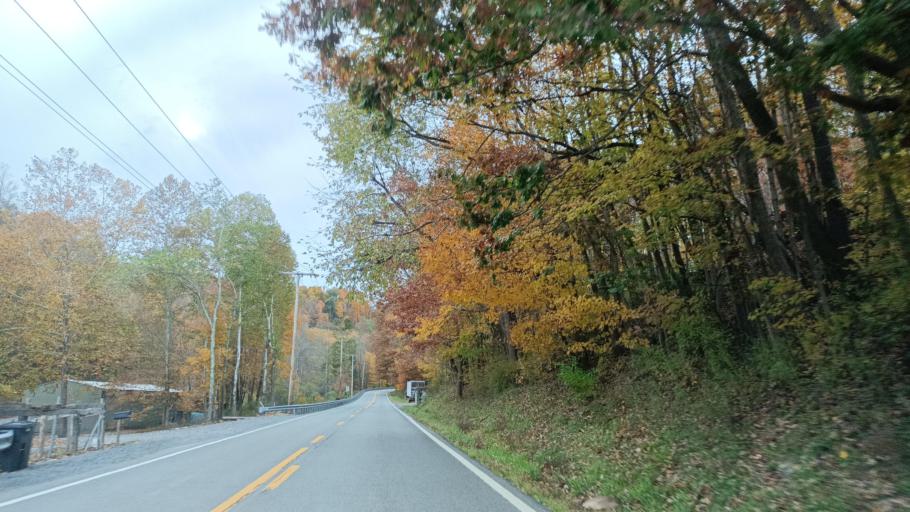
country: US
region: West Virginia
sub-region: Taylor County
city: Grafton
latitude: 39.3300
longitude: -79.9078
